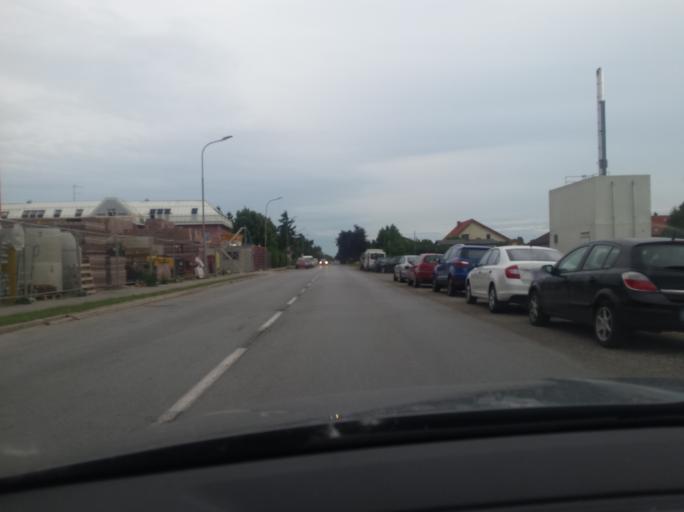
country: AT
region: Lower Austria
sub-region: Politischer Bezirk Ganserndorf
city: Deutsch-Wagram
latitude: 48.3194
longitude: 16.5799
